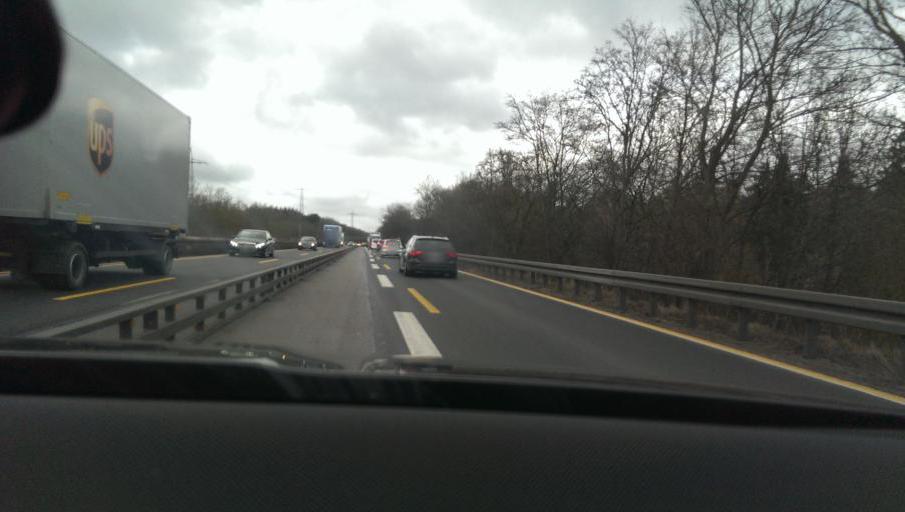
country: DE
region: Hesse
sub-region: Regierungsbezirk Kassel
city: Petersberg
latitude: 50.5872
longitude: 9.6989
